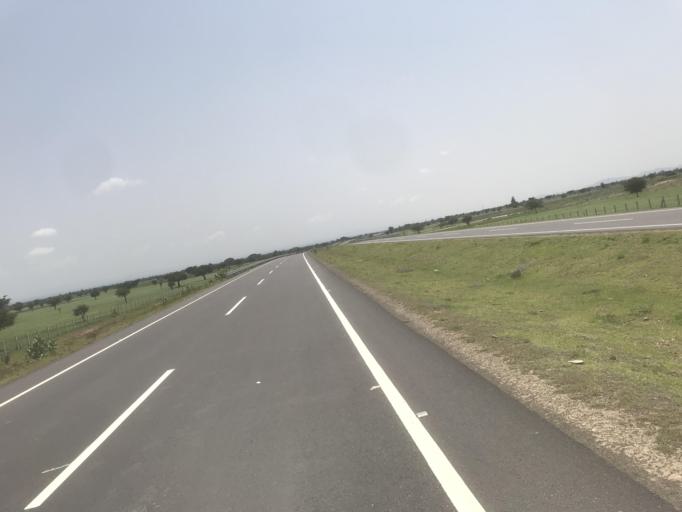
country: ET
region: Oromiya
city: Mojo
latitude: 8.2827
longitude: 38.9164
